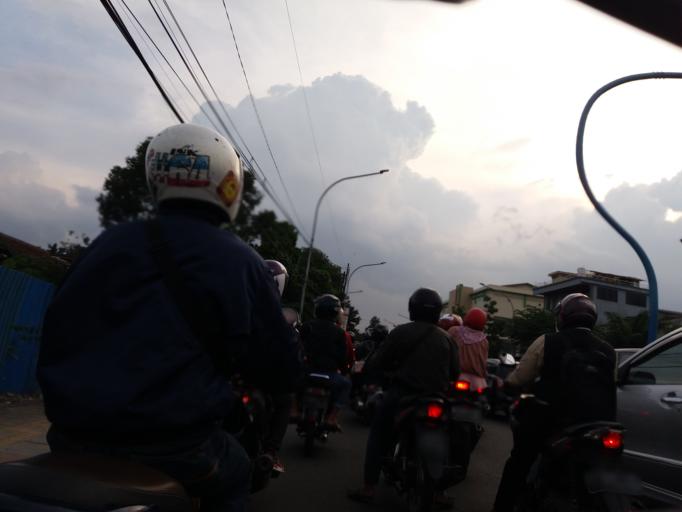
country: ID
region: West Java
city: Bandung
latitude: -6.9139
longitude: 107.6426
